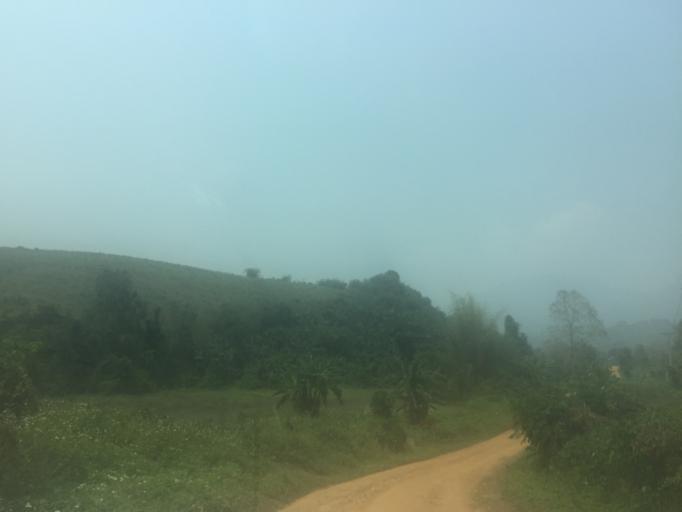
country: TH
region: Phayao
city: Phu Sang
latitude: 19.7708
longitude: 100.5331
